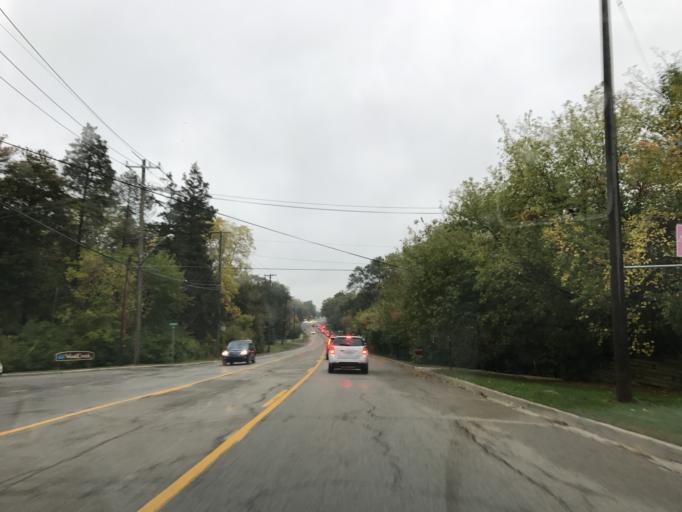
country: US
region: Michigan
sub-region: Oakland County
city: Franklin
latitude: 42.4999
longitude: -83.3253
